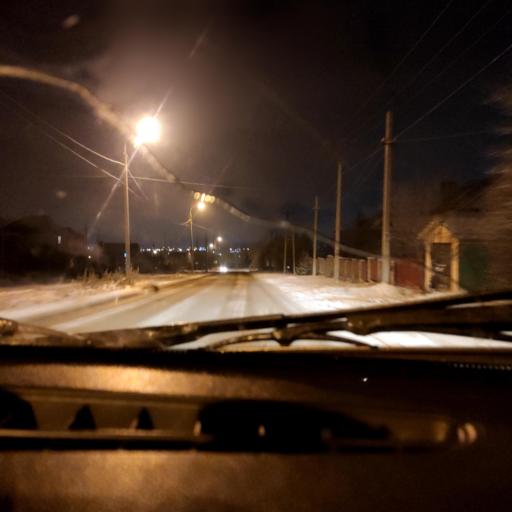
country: RU
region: Bashkortostan
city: Ufa
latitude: 54.6031
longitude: 55.9482
